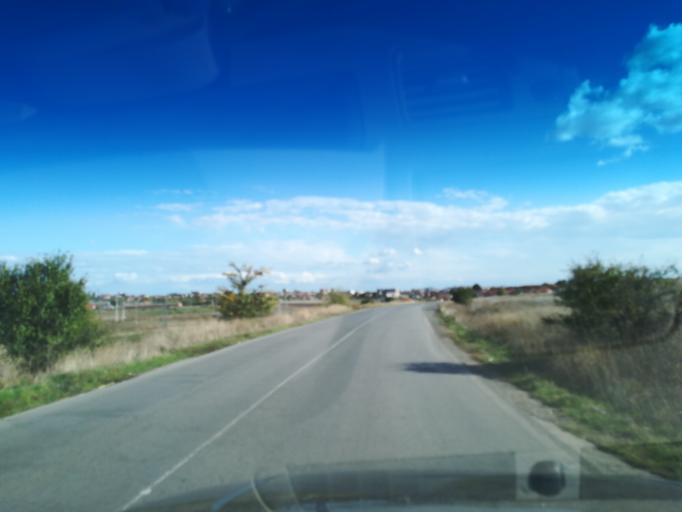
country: BG
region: Stara Zagora
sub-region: Obshtina Chirpan
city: Chirpan
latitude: 42.2065
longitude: 25.3059
